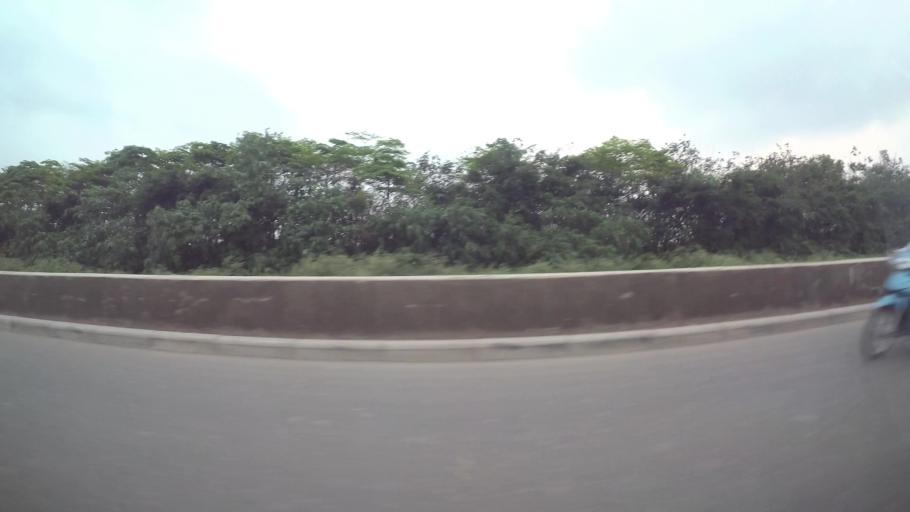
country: VN
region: Ha Noi
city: Hoan Kiem
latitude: 21.0229
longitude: 105.8875
